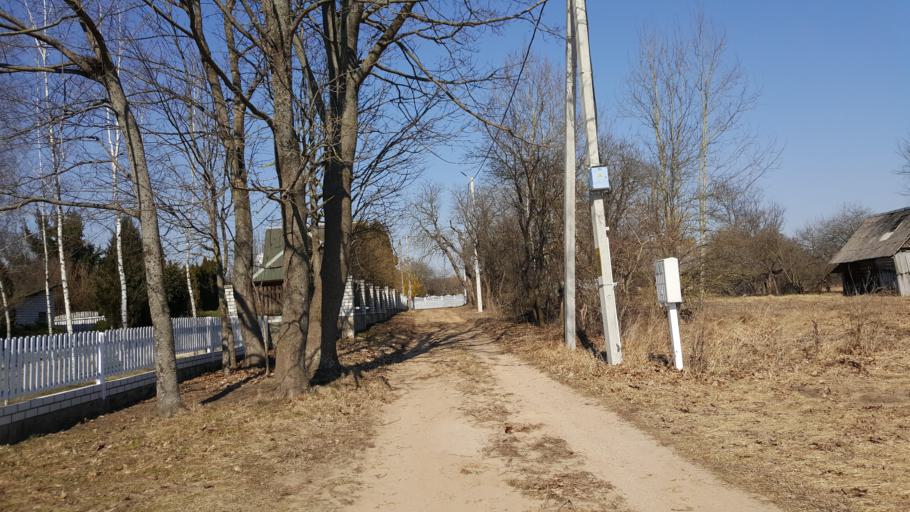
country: BY
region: Brest
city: Kamyanyets
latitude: 52.3617
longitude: 23.7630
